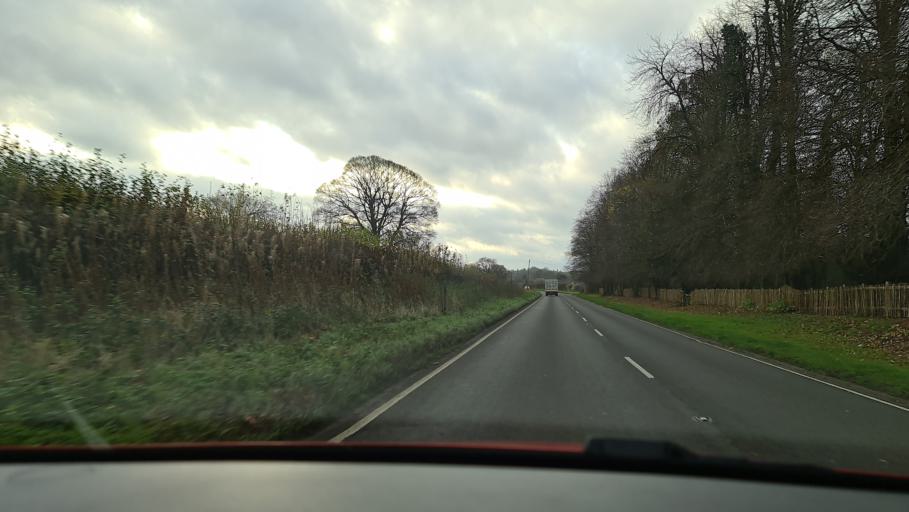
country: GB
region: England
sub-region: Buckinghamshire
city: Great Missenden
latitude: 51.7304
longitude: -0.7270
